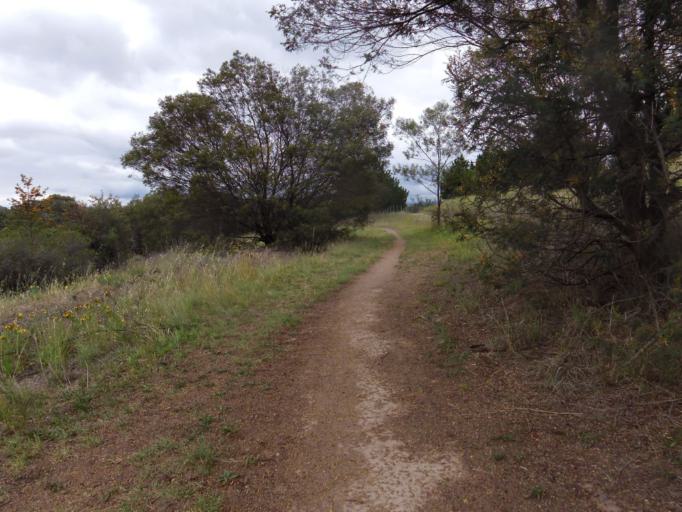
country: AU
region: Australian Capital Territory
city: Macquarie
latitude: -35.3396
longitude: 149.0276
